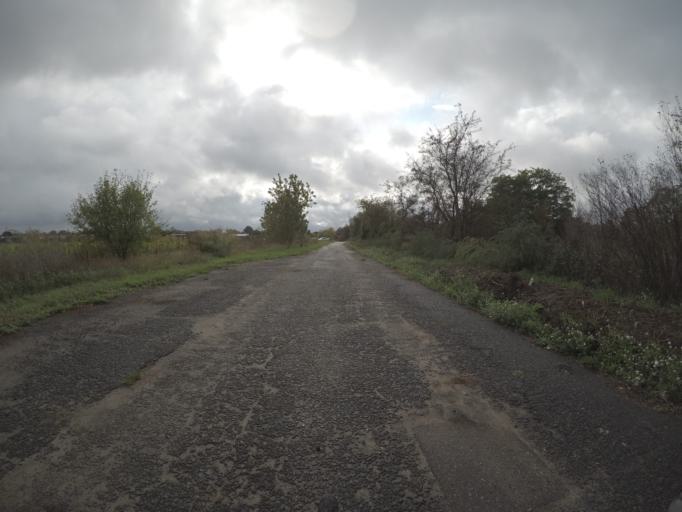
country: DE
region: Berlin
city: Blankenfelde
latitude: 52.6626
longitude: 13.3880
